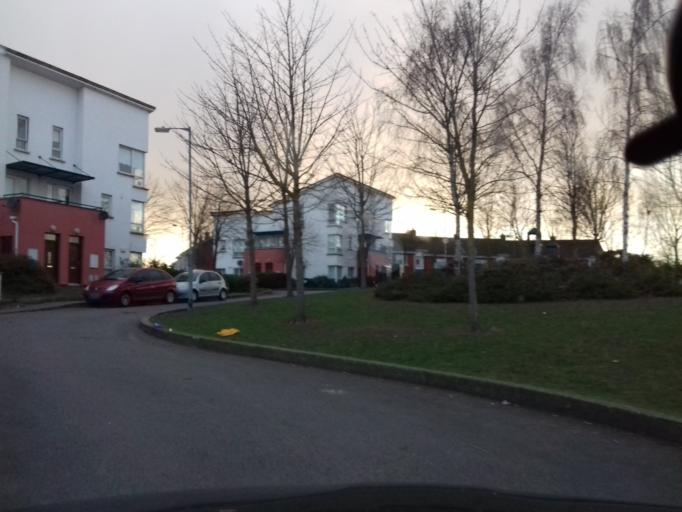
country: IE
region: Leinster
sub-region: Fingal County
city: Blanchardstown
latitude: 53.4024
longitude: -6.3890
